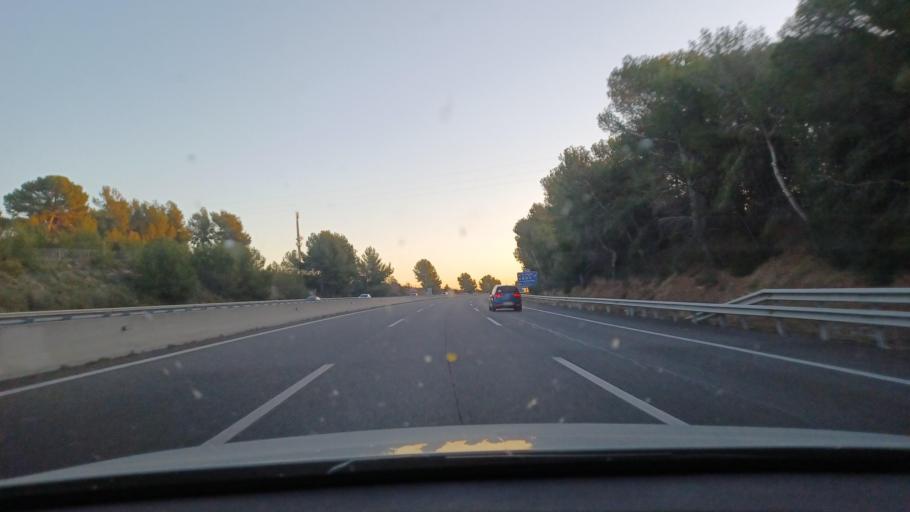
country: ES
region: Catalonia
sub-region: Provincia de Tarragona
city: Sant Jaume dels Domenys
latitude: 41.2858
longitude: 1.5802
